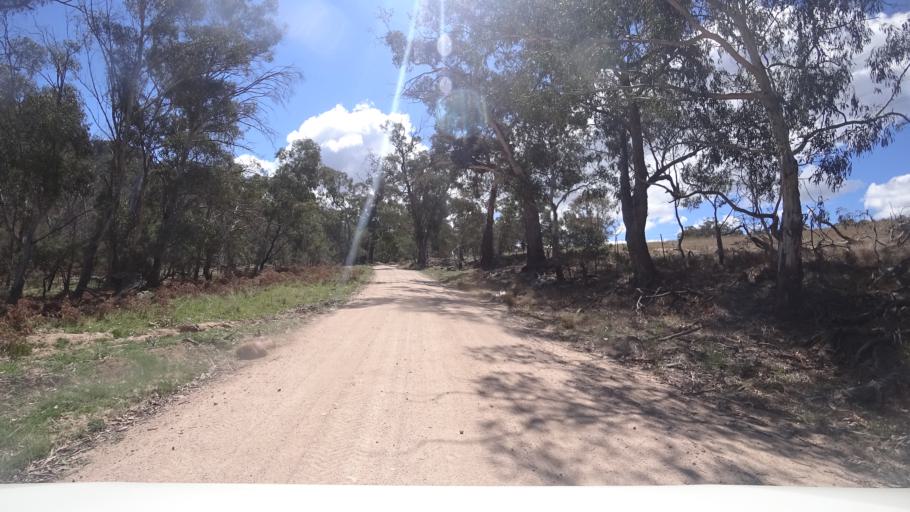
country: AU
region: New South Wales
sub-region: Oberon
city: Oberon
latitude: -33.5481
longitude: 149.9318
